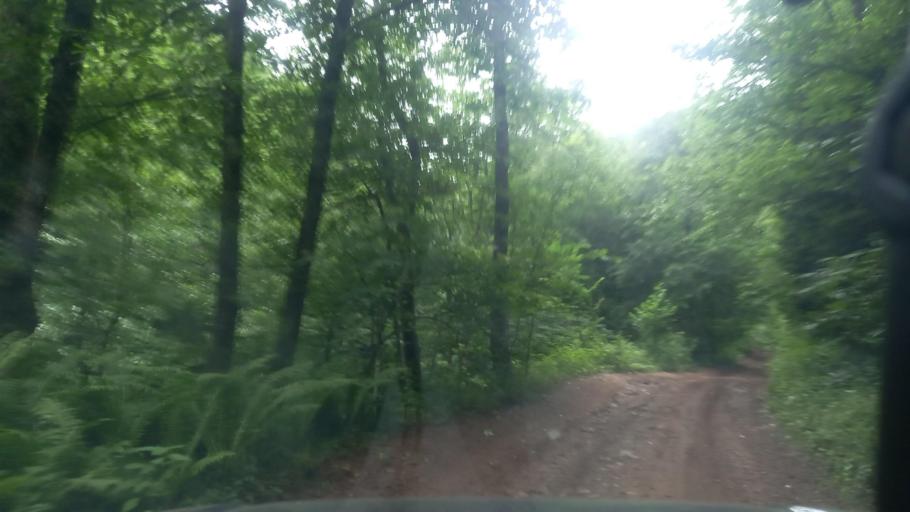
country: RU
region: Karachayevo-Cherkesiya
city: Kurdzhinovo
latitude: 43.8113
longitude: 40.8736
